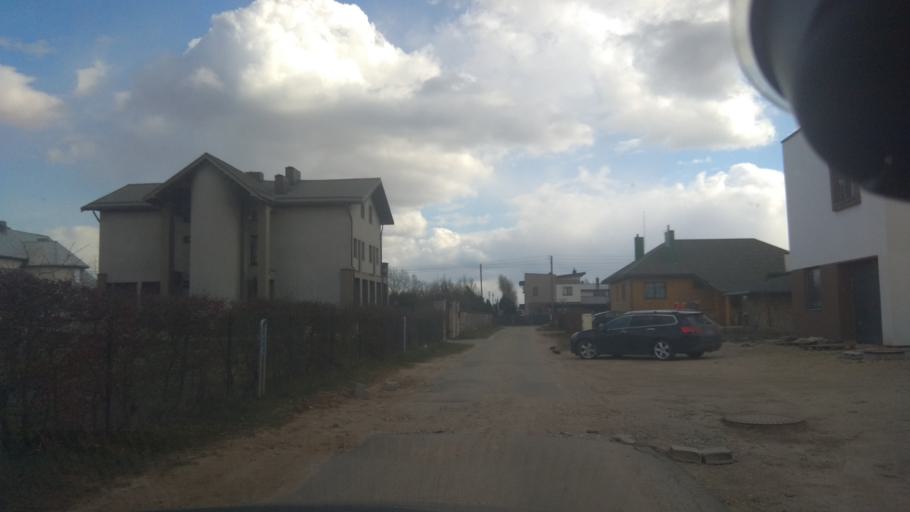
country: LT
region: Vilnius County
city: Pasilaiciai
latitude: 54.7440
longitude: 25.1992
